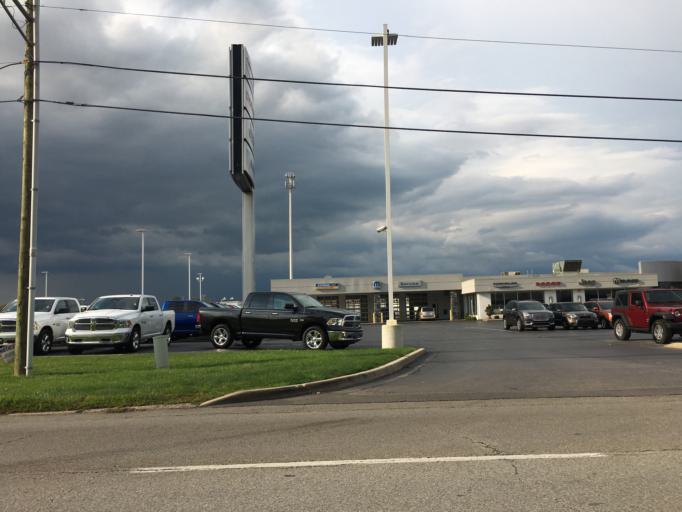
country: US
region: Indiana
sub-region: Howard County
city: Kokomo
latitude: 40.4624
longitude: -86.1172
